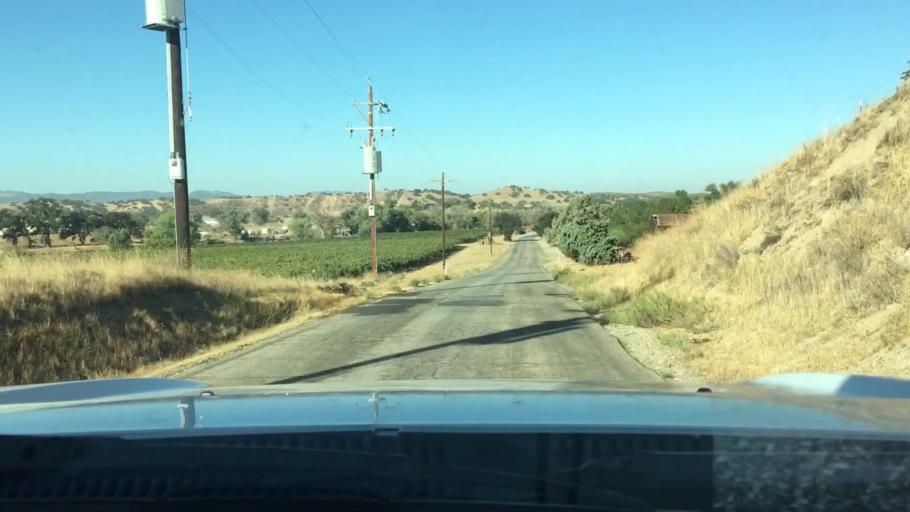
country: US
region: California
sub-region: San Luis Obispo County
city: San Miguel
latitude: 35.7178
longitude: -120.6357
